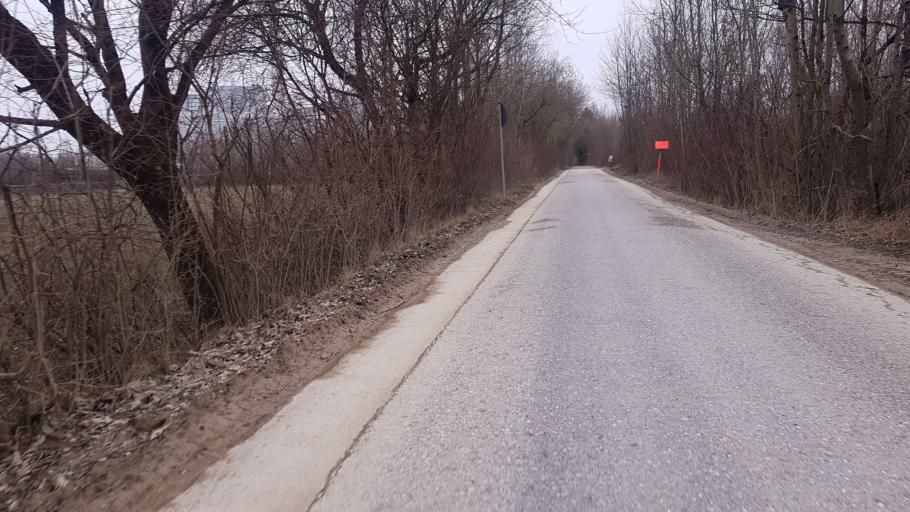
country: DE
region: Bavaria
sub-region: Upper Bavaria
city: Unterfoehring
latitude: 48.1820
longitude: 11.6478
